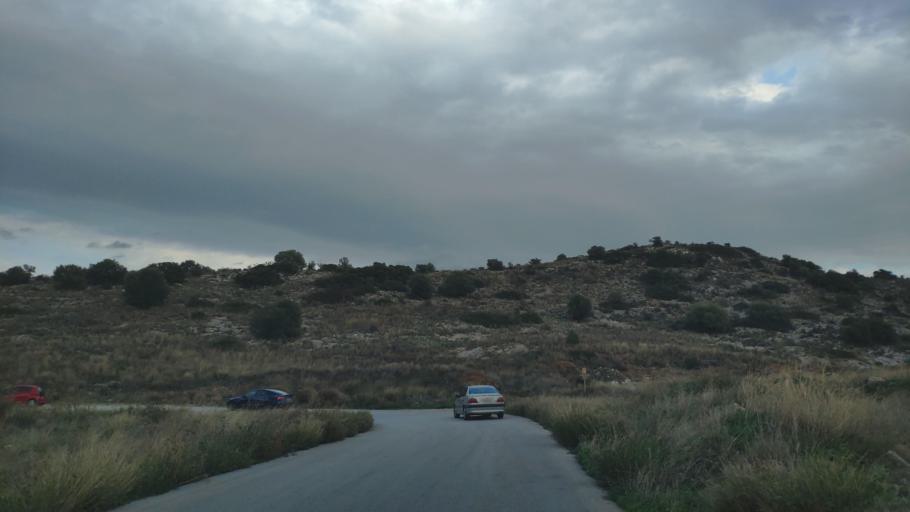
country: GR
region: Attica
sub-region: Nomarchia Dytikis Attikis
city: Megara
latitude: 37.9761
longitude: 23.3723
